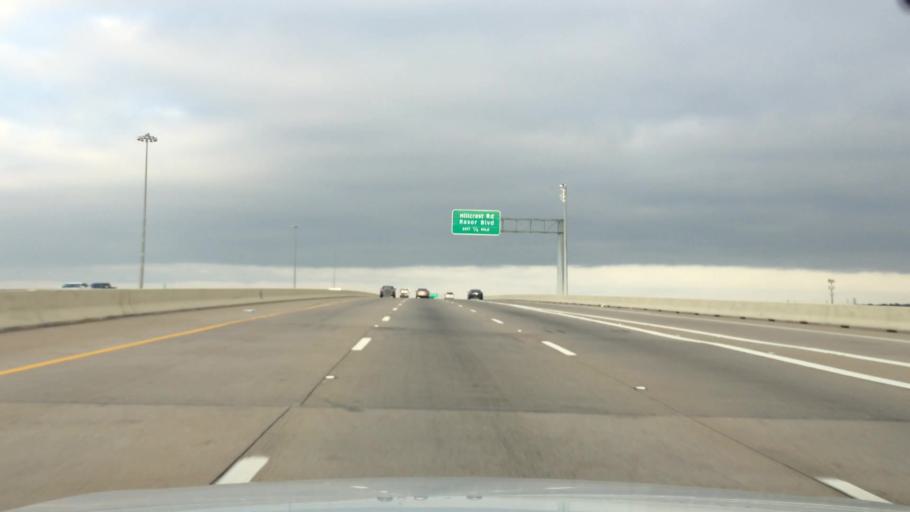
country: US
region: Texas
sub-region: Collin County
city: Frisco
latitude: 33.0963
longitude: -96.8073
